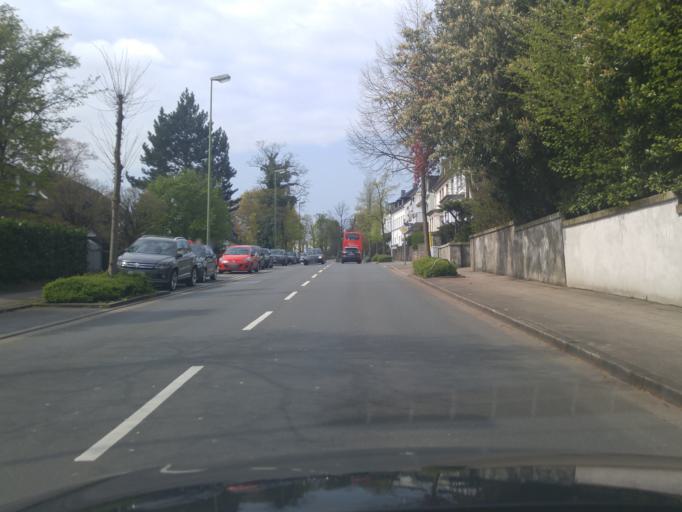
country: DE
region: North Rhine-Westphalia
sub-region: Regierungsbezirk Dusseldorf
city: Essen
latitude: 51.4166
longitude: 7.0064
